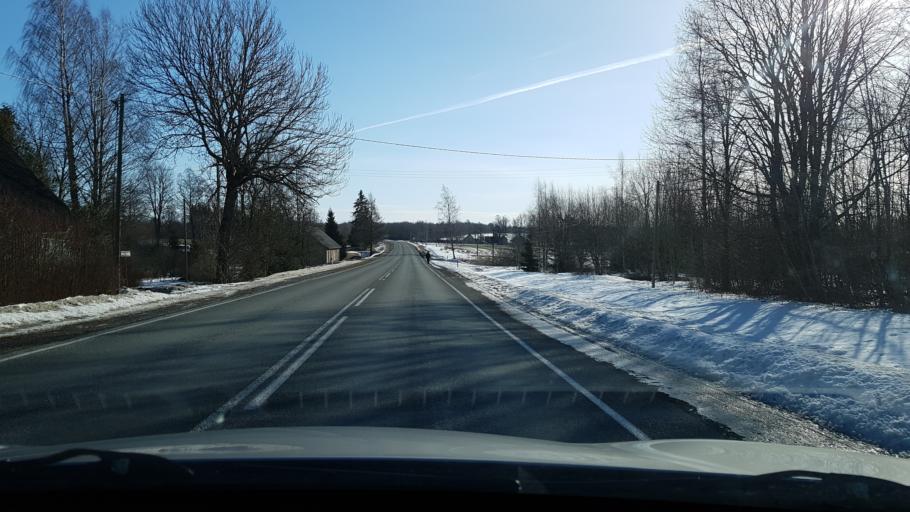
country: EE
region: Viljandimaa
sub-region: Suure-Jaani vald
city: Suure-Jaani
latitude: 58.5540
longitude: 25.4489
